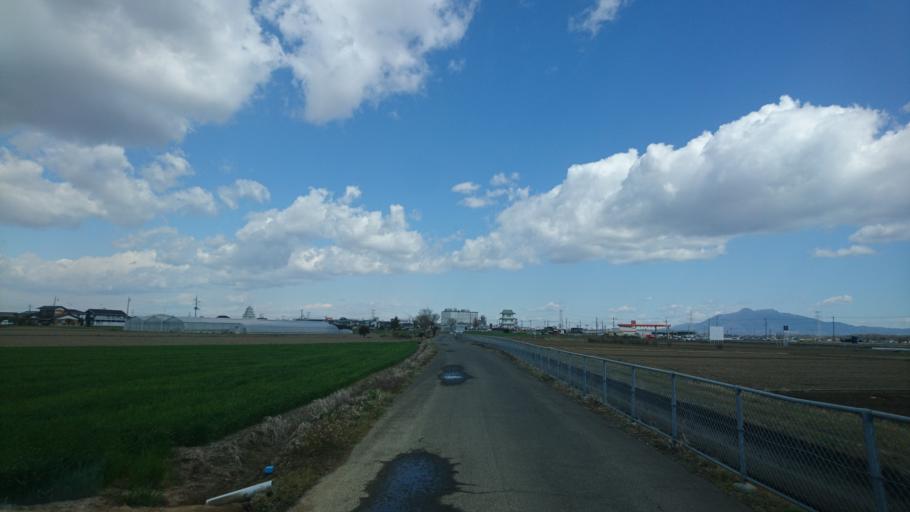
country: JP
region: Ibaraki
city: Ishige
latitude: 36.1007
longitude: 139.9827
